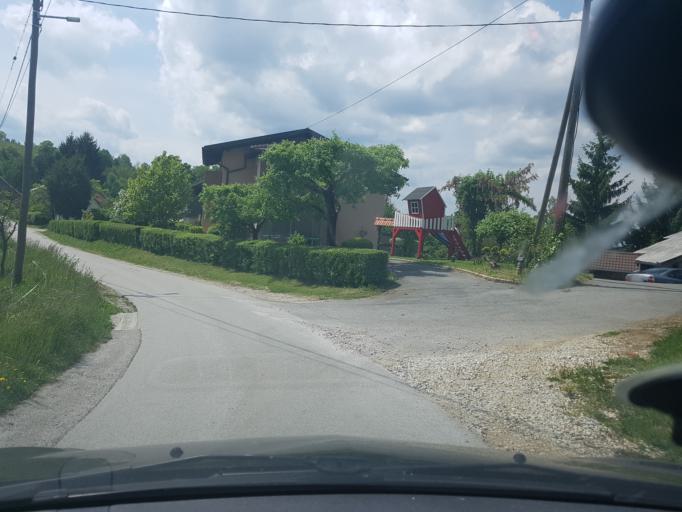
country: SI
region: Rogatec
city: Rogatec
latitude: 46.2142
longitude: 15.7002
